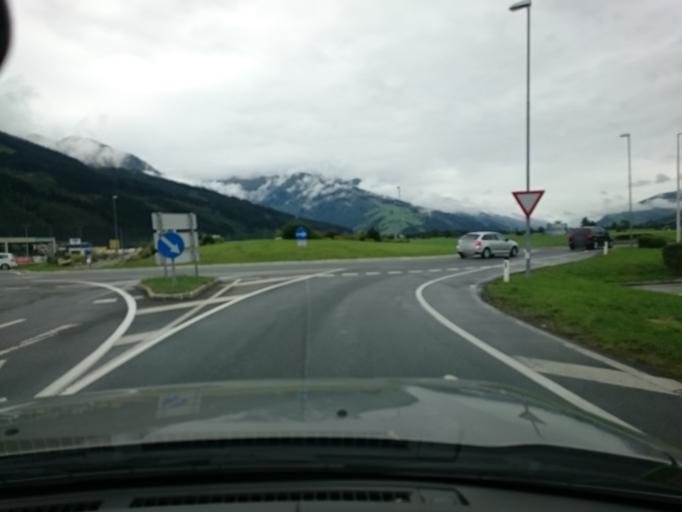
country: AT
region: Salzburg
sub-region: Politischer Bezirk Zell am See
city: Bruck an der Grossglocknerstrasse
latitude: 47.2887
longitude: 12.8092
